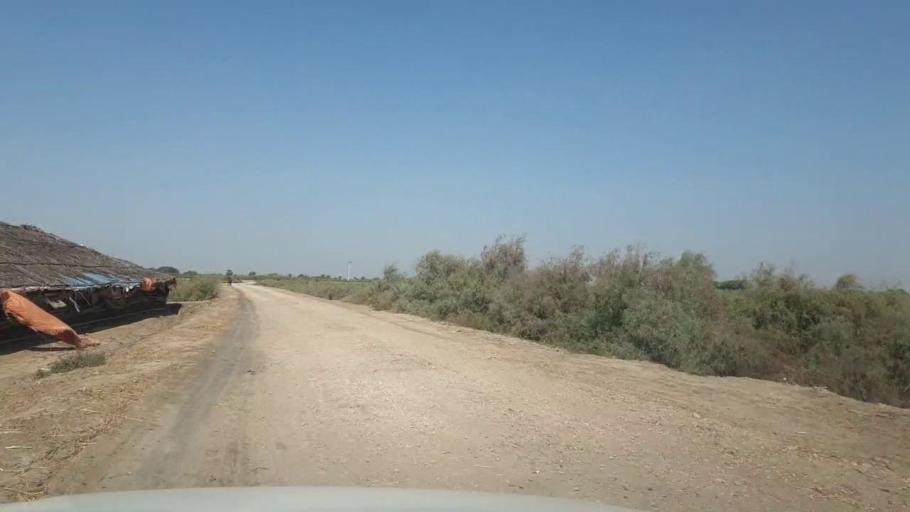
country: PK
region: Sindh
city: Chuhar Jamali
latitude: 24.3806
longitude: 67.8023
